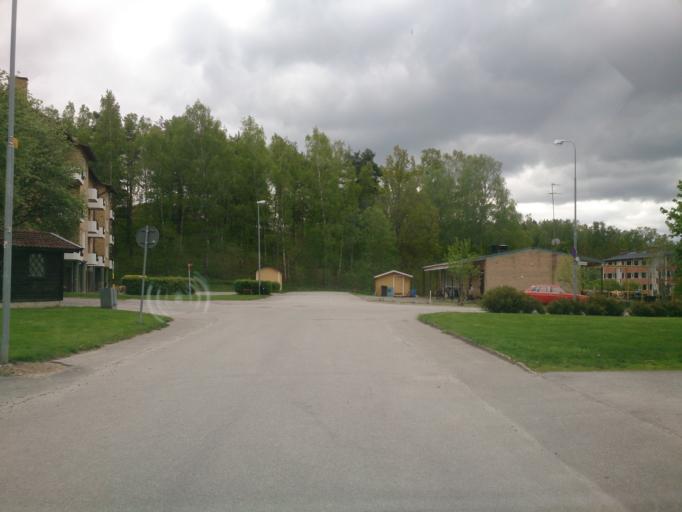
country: SE
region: OEstergoetland
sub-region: Atvidabergs Kommun
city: Atvidaberg
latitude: 58.2041
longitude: 16.0105
